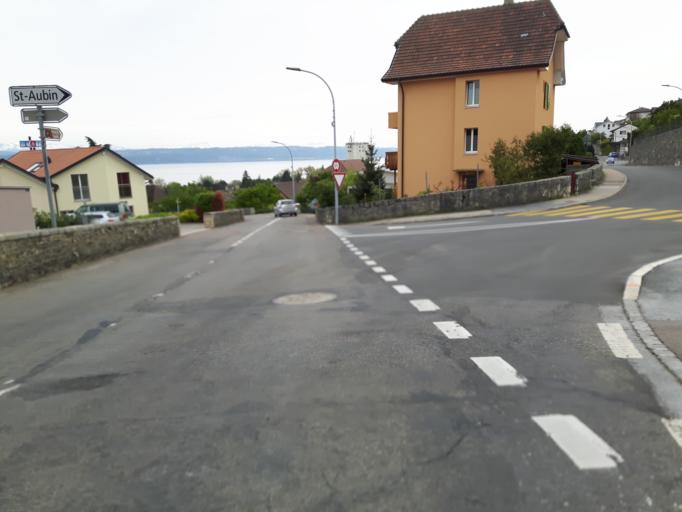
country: CH
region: Neuchatel
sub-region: Boudry District
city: Gorgier
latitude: 46.9016
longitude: 6.7800
